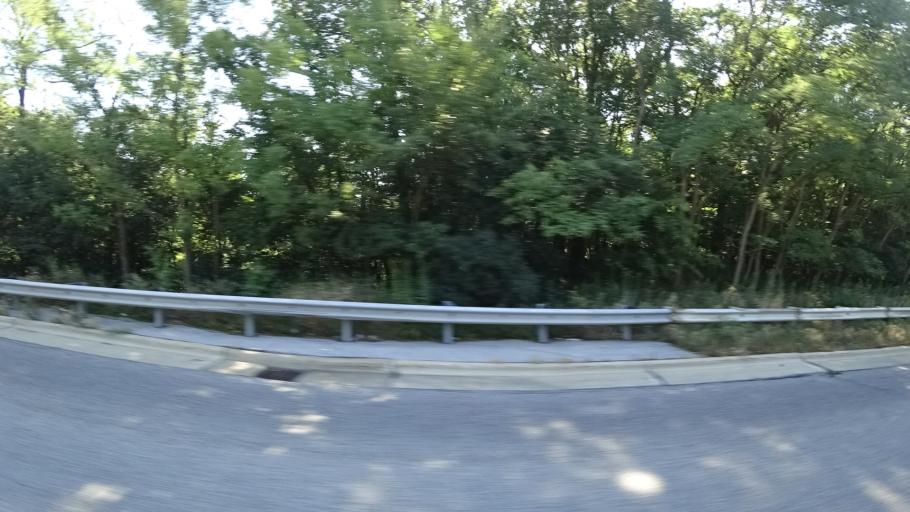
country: US
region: Illinois
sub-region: Cook County
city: Palos Heights
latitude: 41.6284
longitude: -87.7954
